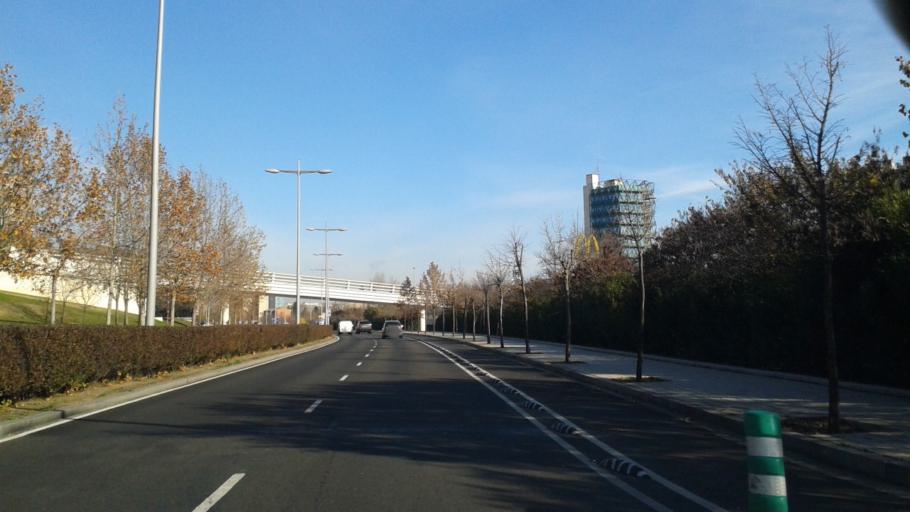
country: ES
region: Castille and Leon
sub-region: Provincia de Valladolid
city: Valladolid
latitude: 41.6359
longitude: -4.7478
